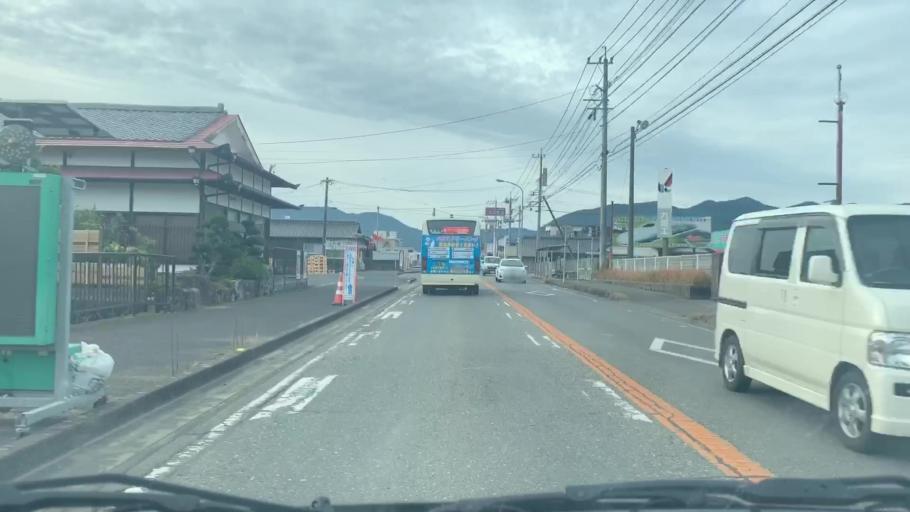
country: JP
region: Saga Prefecture
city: Ureshinomachi-shimojuku
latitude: 33.1080
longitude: 129.9981
